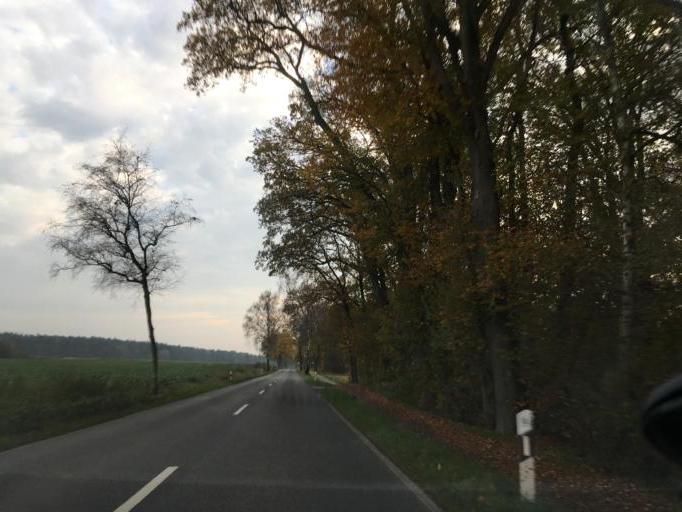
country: DE
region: Lower Saxony
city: Wietzendorf
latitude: 52.8939
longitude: 9.9841
